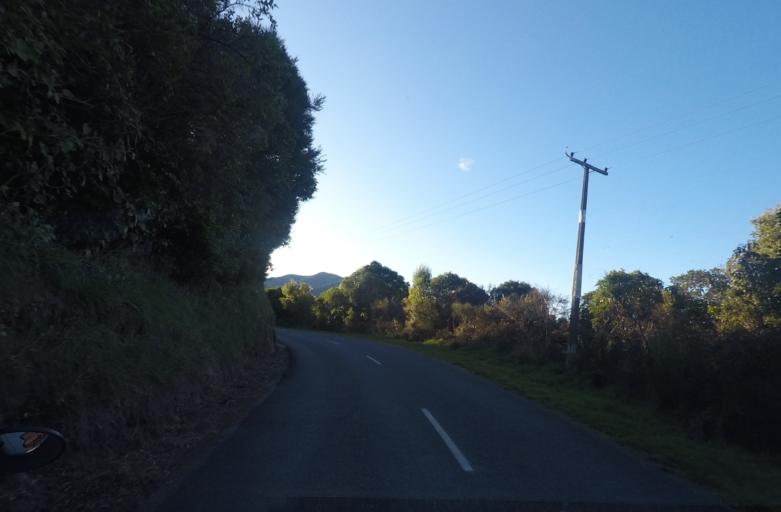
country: NZ
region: Marlborough
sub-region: Marlborough District
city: Picton
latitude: -41.2700
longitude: 173.9582
